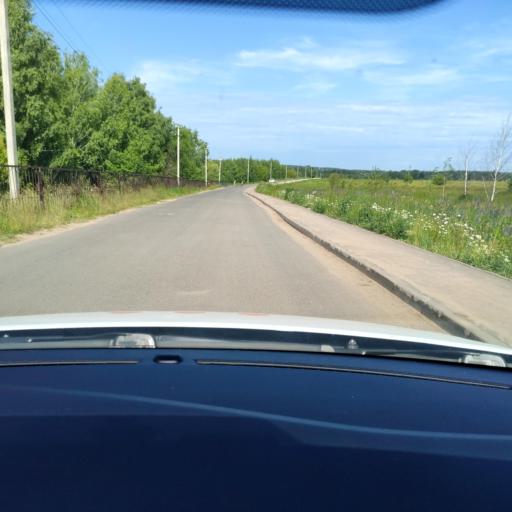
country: RU
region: Tatarstan
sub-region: Gorod Kazan'
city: Kazan
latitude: 55.8900
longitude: 49.0958
